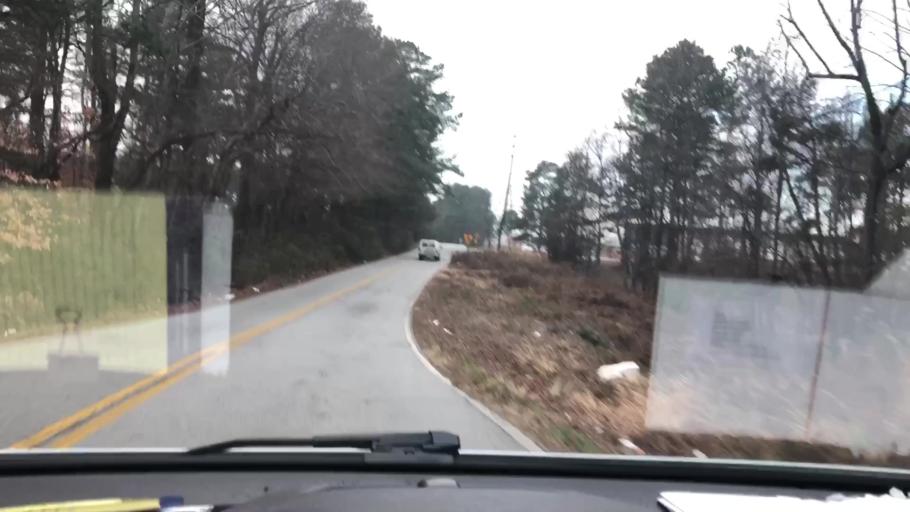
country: US
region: Georgia
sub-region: Gwinnett County
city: Berkeley Lake
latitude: 33.9728
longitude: -84.1719
